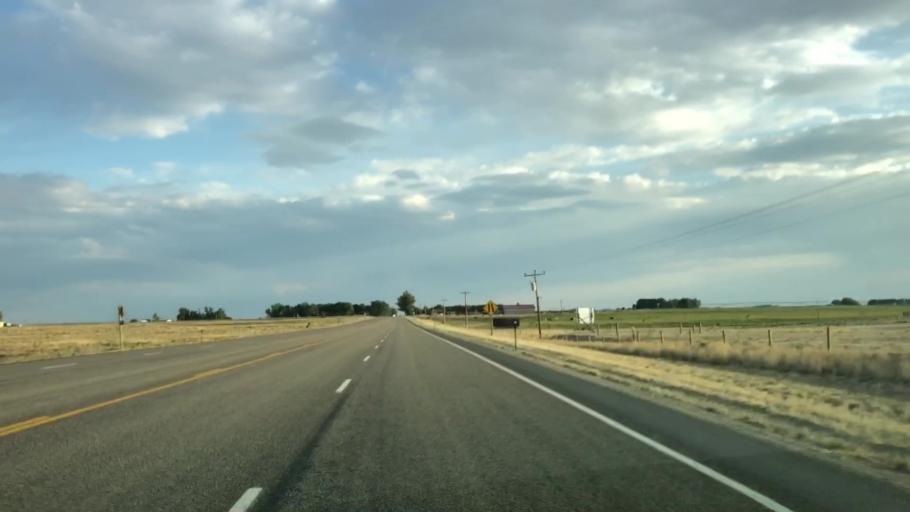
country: US
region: Wyoming
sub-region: Sweetwater County
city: North Rock Springs
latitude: 42.0645
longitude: -109.4381
